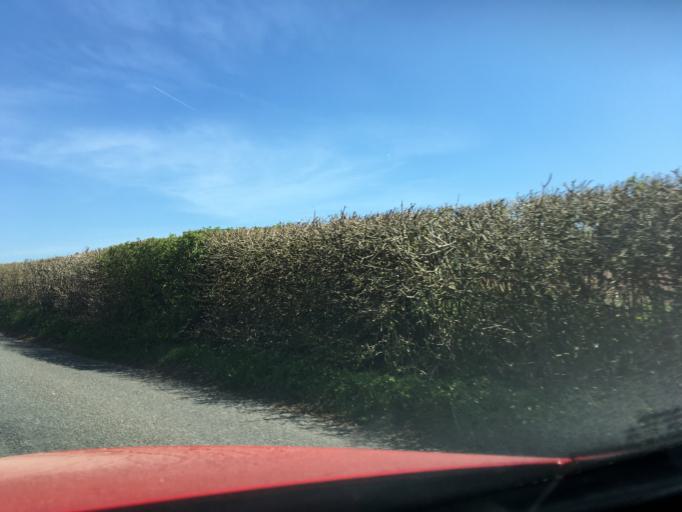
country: GB
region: Wales
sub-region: Monmouthshire
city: Llangwm
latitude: 51.7238
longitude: -2.8355
